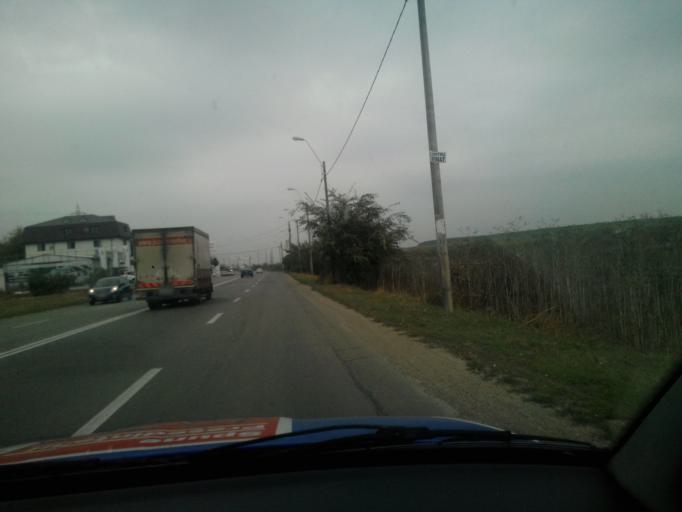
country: RO
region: Braila
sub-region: Municipiul Braila
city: Braila
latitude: 45.2964
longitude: 27.9830
